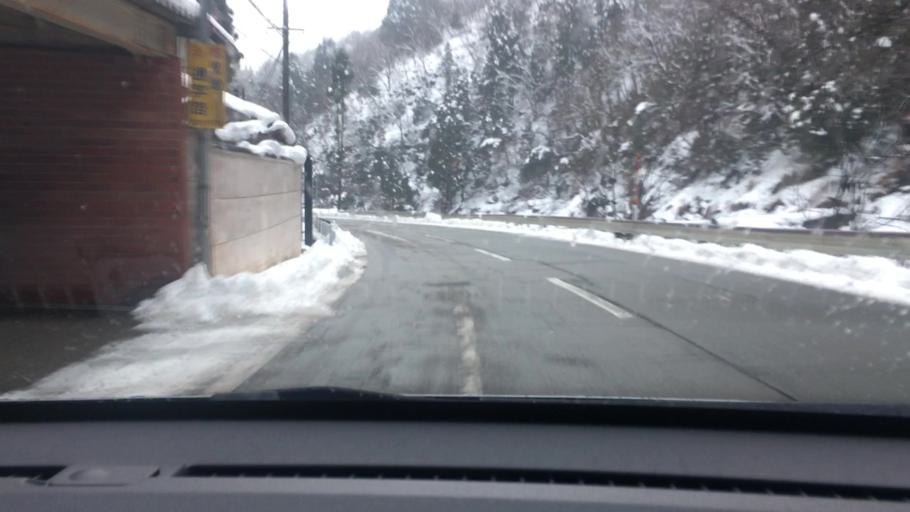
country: JP
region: Hyogo
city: Toyooka
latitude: 35.3706
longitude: 134.5771
